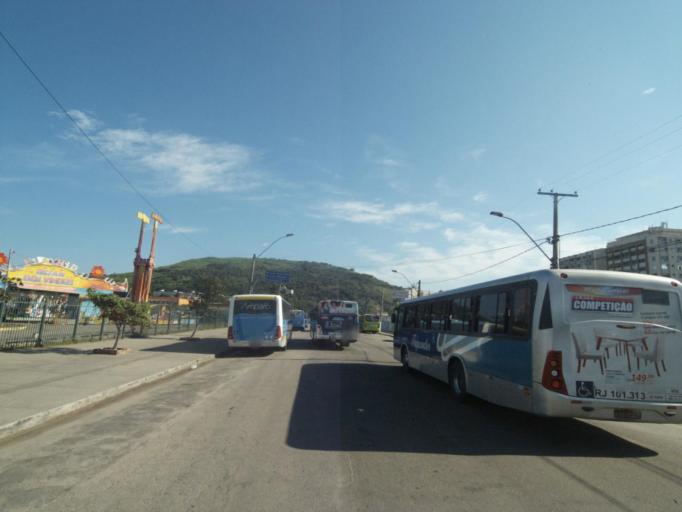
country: BR
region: Rio de Janeiro
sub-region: Niteroi
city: Niteroi
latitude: -22.8888
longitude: -43.1253
